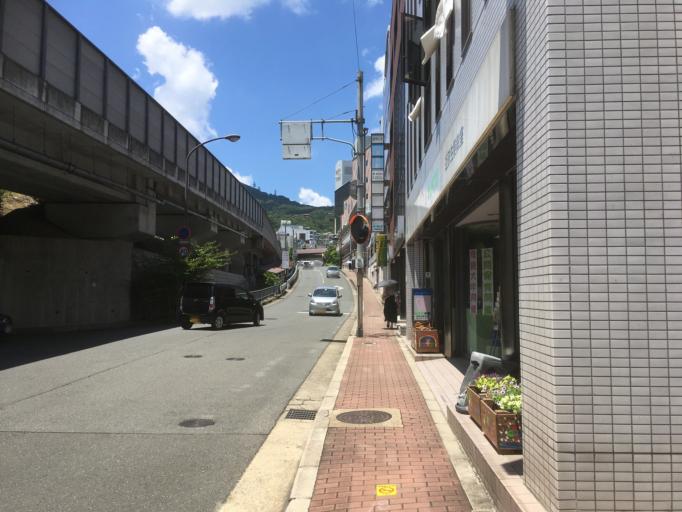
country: JP
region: Nara
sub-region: Ikoma-shi
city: Ikoma
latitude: 34.6936
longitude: 135.7002
